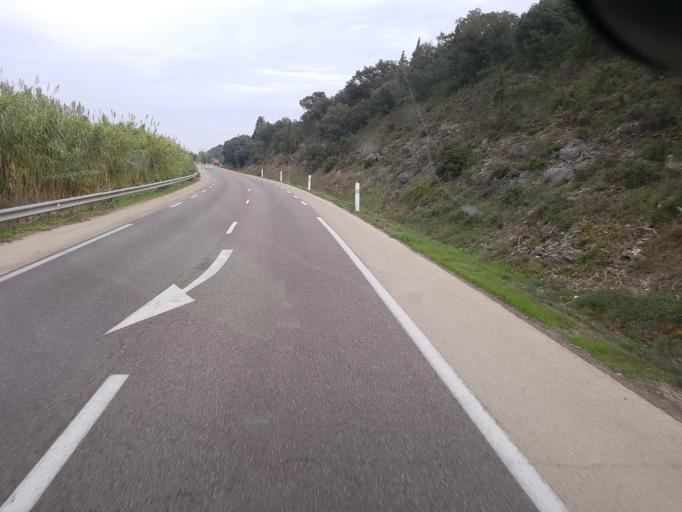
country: FR
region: Languedoc-Roussillon
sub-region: Departement du Gard
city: Aramon
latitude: 43.8957
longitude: 4.7102
